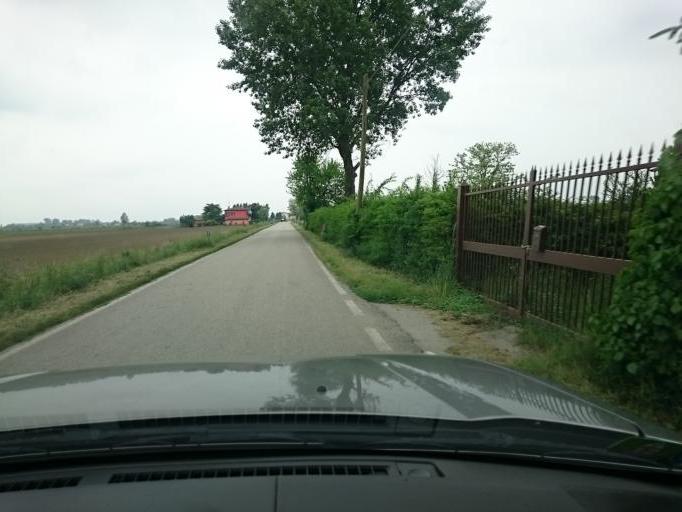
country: IT
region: Veneto
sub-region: Provincia di Padova
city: Casalserugo
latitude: 45.2839
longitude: 11.9062
